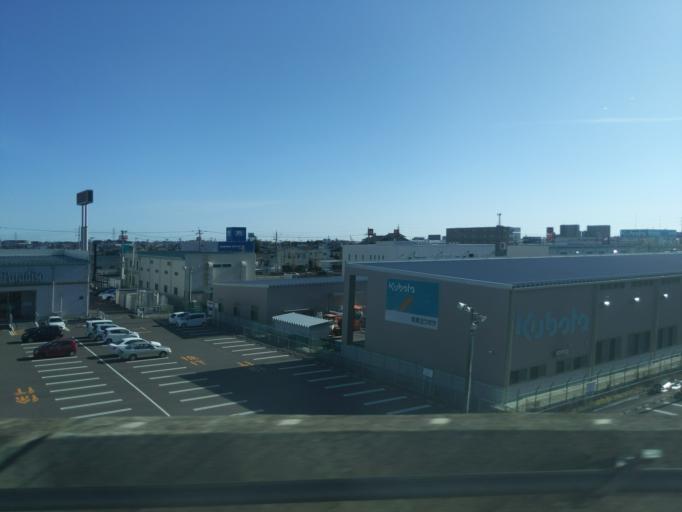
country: JP
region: Miyagi
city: Sendai
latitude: 38.1819
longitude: 140.8738
